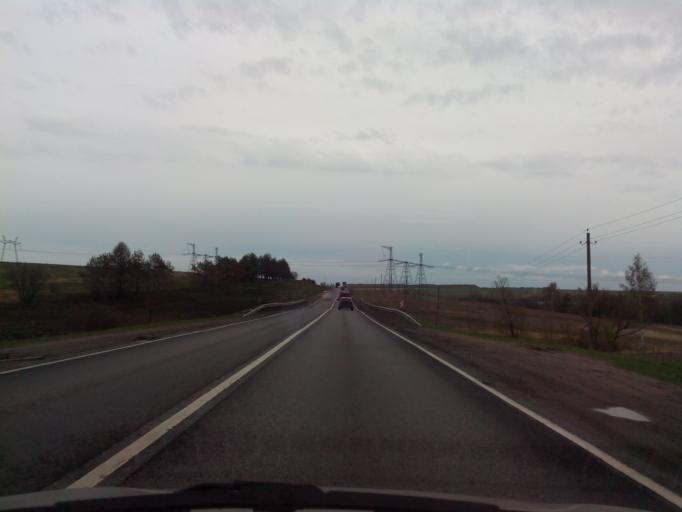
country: RU
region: Moskovskaya
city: Ozherel'ye
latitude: 54.7302
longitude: 38.2642
